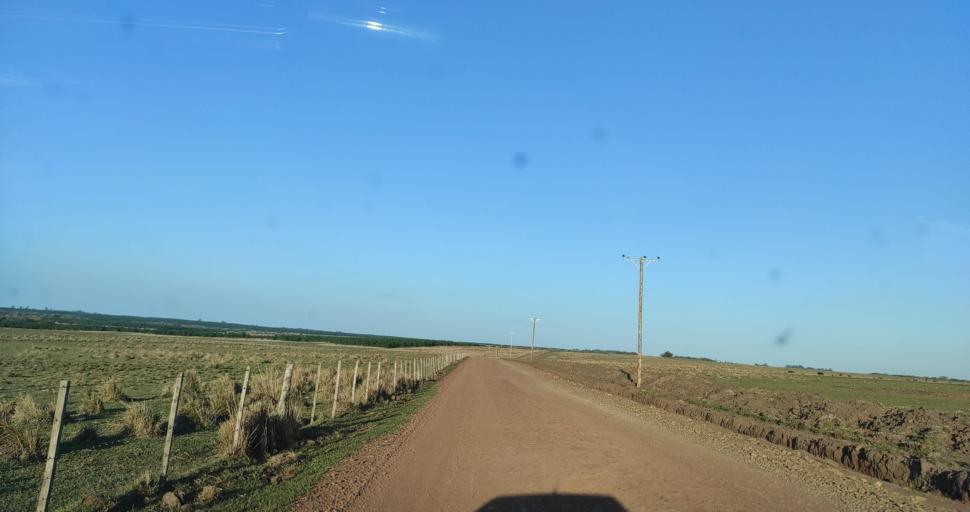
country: PY
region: Itapua
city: Carmen del Parana
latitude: -27.4116
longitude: -56.1462
